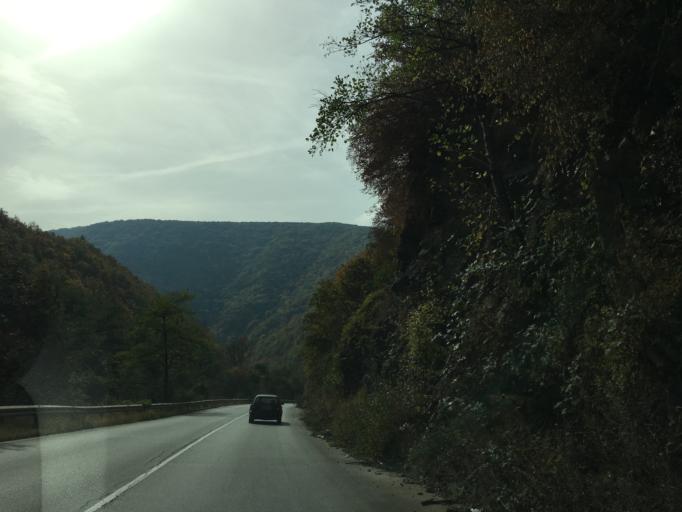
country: BG
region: Sofia-Capital
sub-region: Stolichna Obshtina
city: Sofia
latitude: 42.5635
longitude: 23.4248
